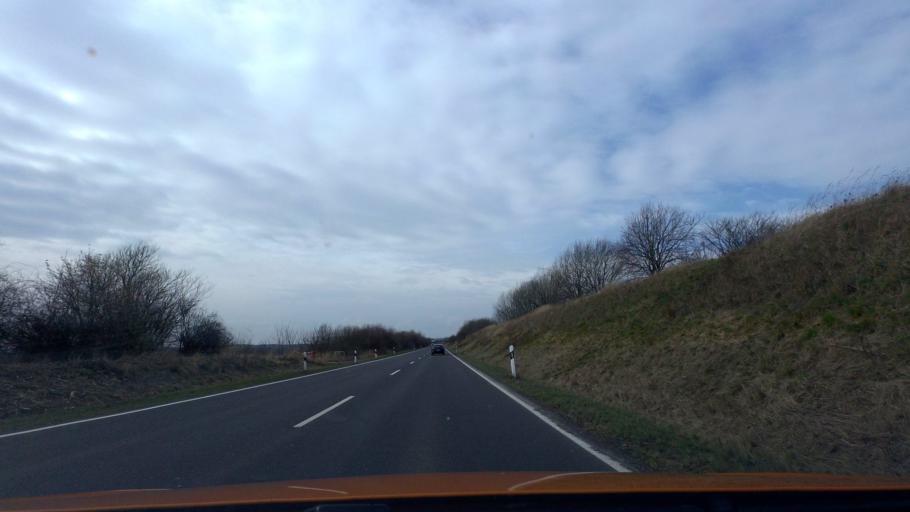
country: DE
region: Lower Saxony
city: Helmstedt
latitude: 52.2147
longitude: 11.0157
